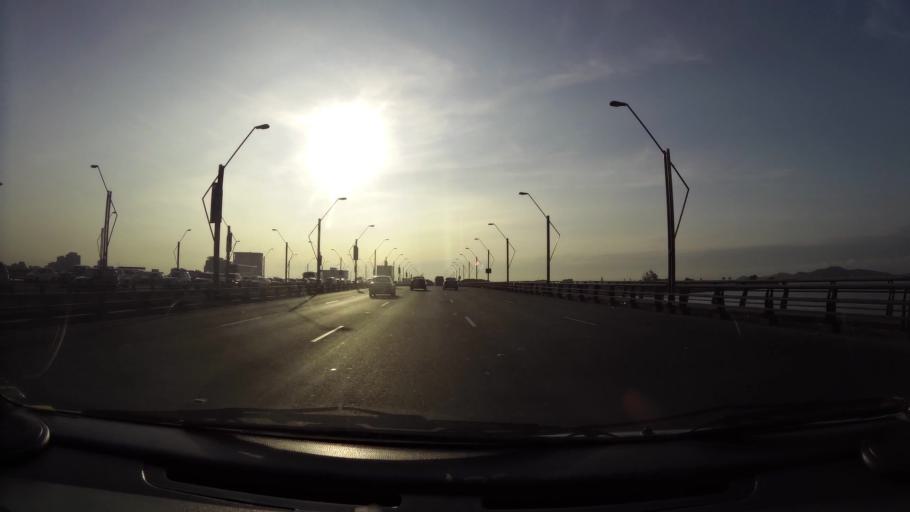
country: EC
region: Guayas
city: Eloy Alfaro
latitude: -2.1536
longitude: -79.8741
